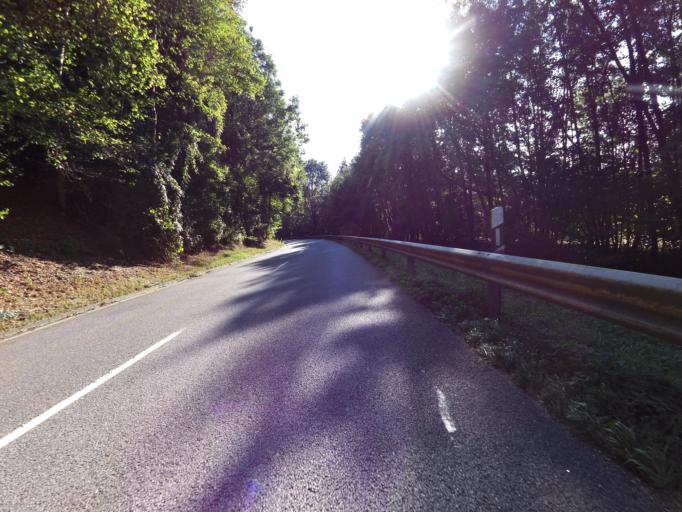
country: DE
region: Bavaria
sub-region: Lower Bavaria
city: Niederaichbach
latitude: 48.6014
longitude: 12.3021
